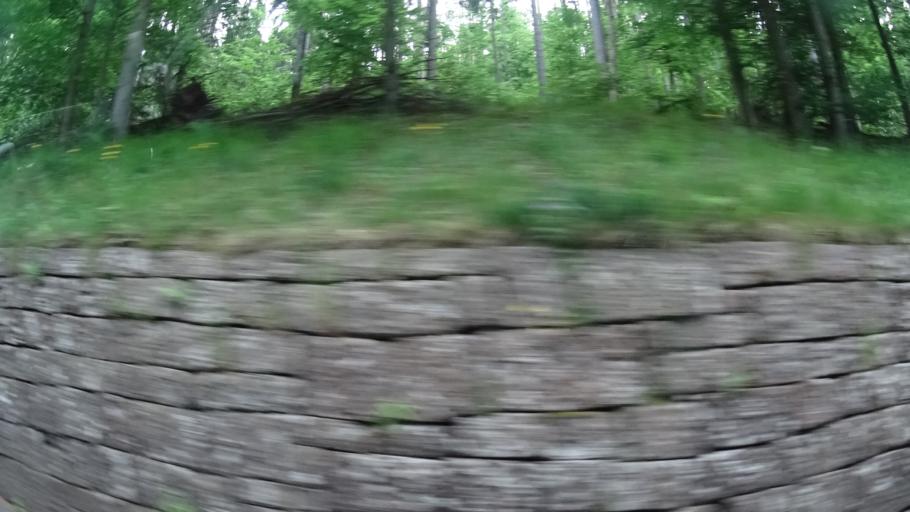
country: DE
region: Bavaria
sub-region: Regierungsbezirk Unterfranken
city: Grafendorf
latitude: 50.1280
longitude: 9.7479
